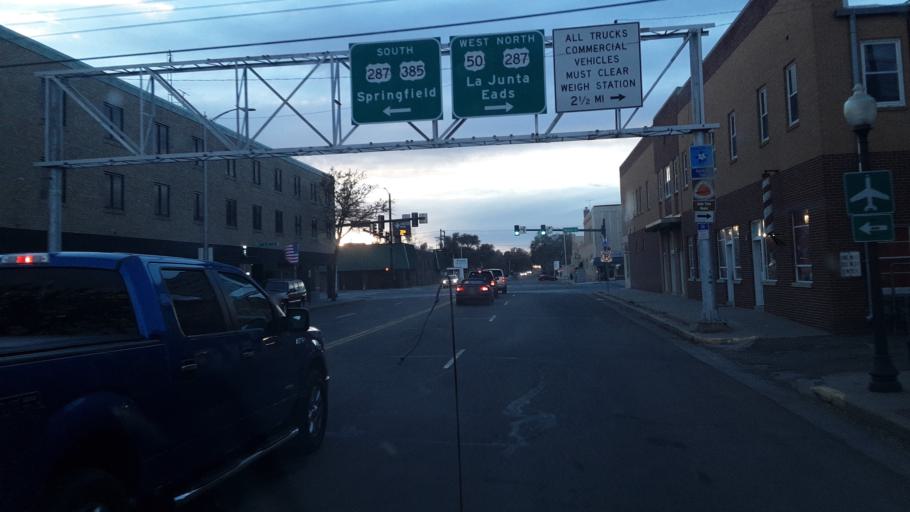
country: US
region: Colorado
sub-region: Prowers County
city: Lamar
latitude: 38.0883
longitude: -102.6183
